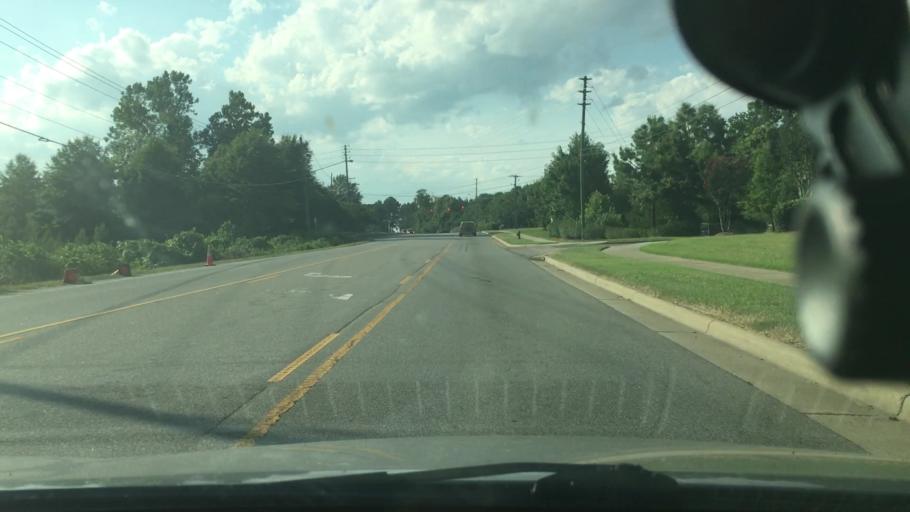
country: US
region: North Carolina
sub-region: Wake County
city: Apex
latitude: 35.7342
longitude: -78.8618
